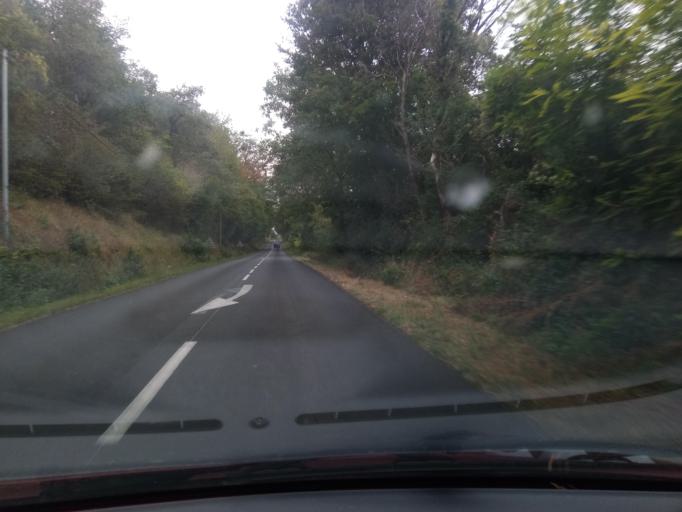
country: FR
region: Poitou-Charentes
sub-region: Departement de la Vienne
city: Pleumartin
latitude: 46.6790
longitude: 0.8294
